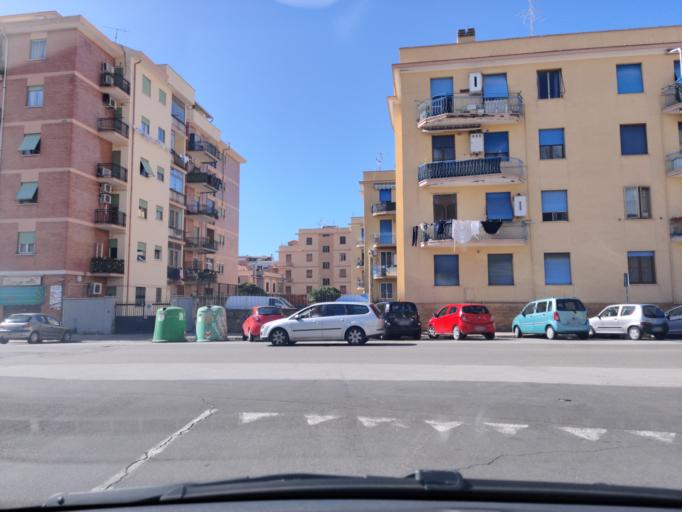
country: IT
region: Latium
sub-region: Citta metropolitana di Roma Capitale
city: Civitavecchia
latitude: 42.0935
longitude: 11.8064
